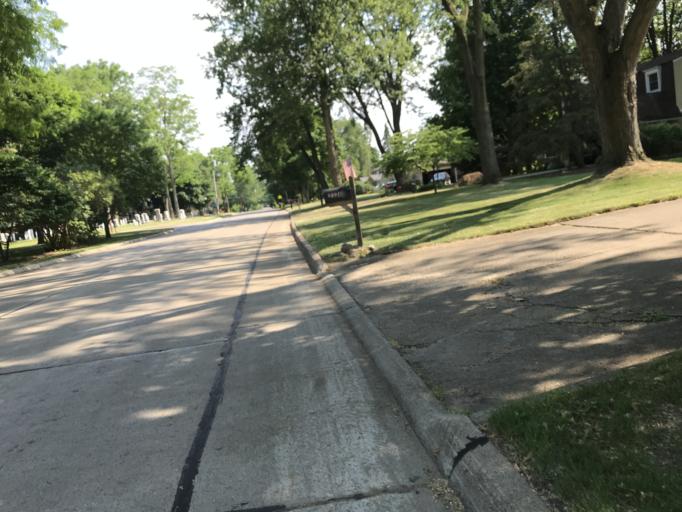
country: US
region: Michigan
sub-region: Oakland County
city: Farmington
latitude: 42.4649
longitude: -83.3863
